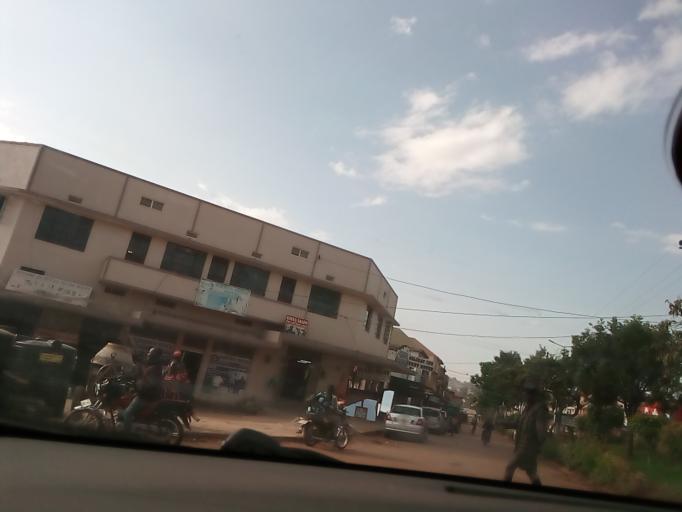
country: UG
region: Central Region
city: Masaka
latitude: -0.3437
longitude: 31.7391
